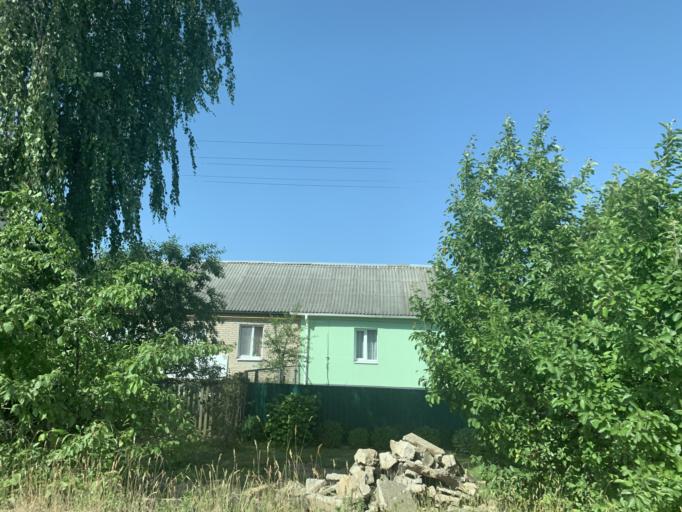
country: BY
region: Minsk
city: Dzyarzhynsk
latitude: 53.6982
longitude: 27.1037
